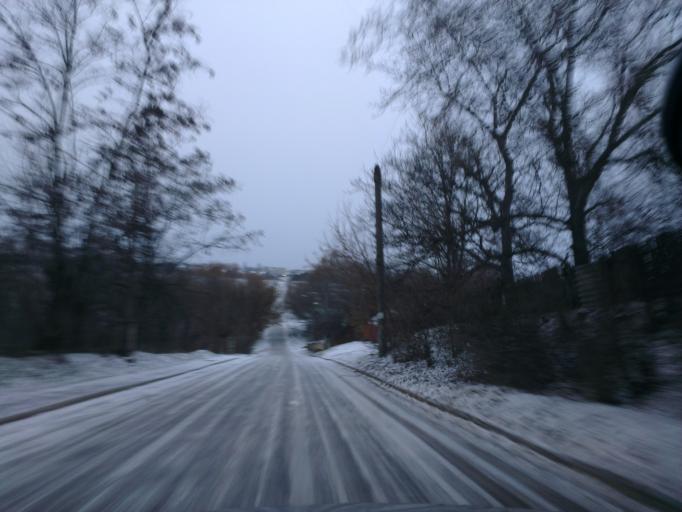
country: MD
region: Chisinau
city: Ciorescu
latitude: 47.1196
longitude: 28.8971
